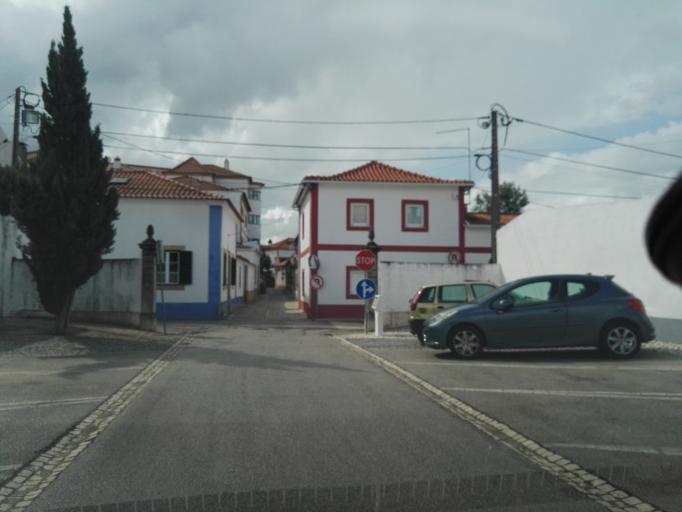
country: PT
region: Santarem
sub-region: Golega
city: Golega
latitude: 39.4044
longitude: -8.4853
